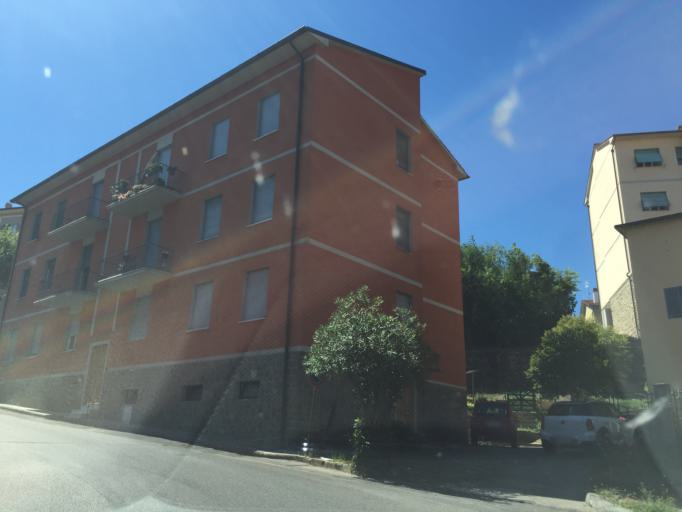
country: IT
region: Tuscany
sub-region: Provincia di Pistoia
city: Pistoia
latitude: 43.9481
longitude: 10.9089
